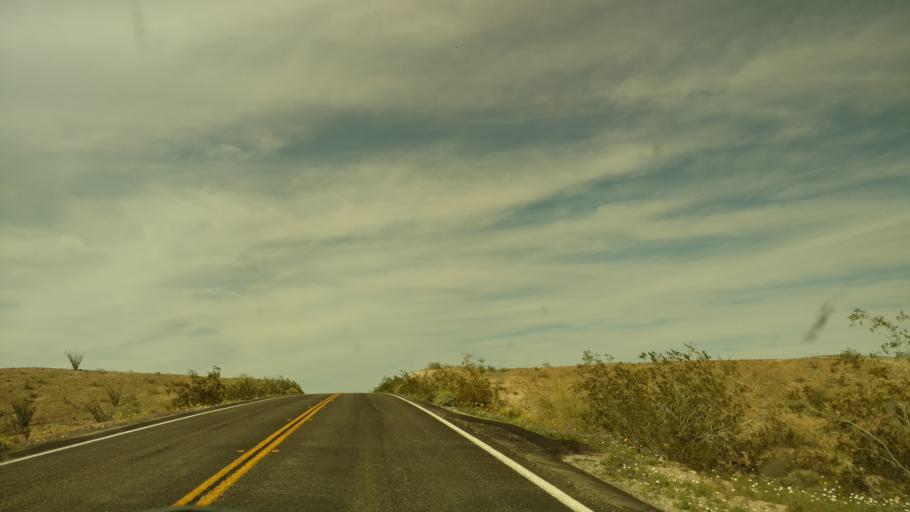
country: US
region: California
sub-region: Riverside County
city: Mesa Verde
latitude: 33.2010
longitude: -114.8575
